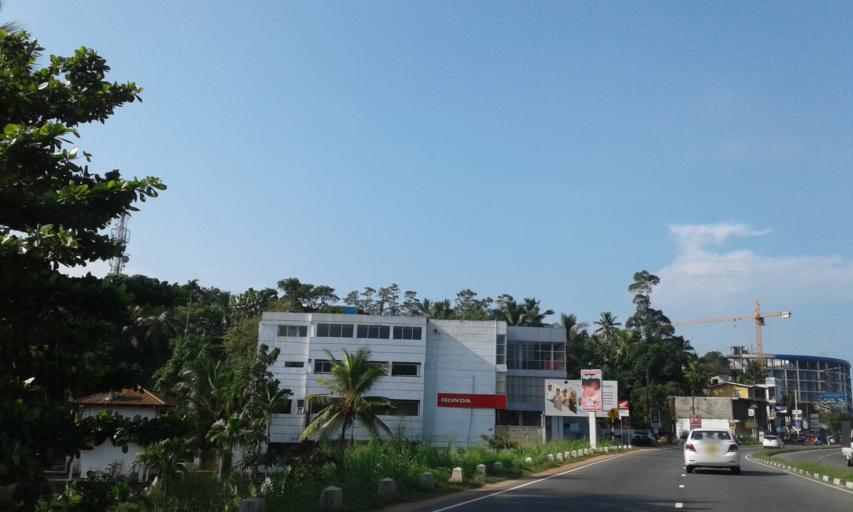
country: LK
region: Western
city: Gampaha
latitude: 7.0330
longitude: 79.9879
